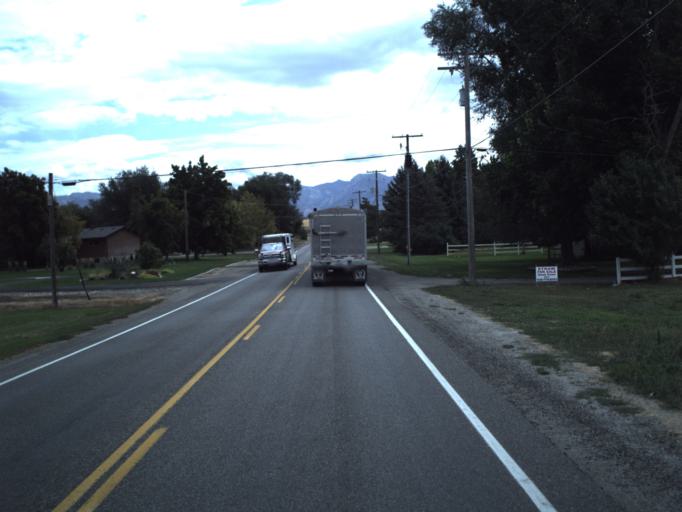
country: US
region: Utah
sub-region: Cache County
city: Benson
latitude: 41.8624
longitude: -111.9876
